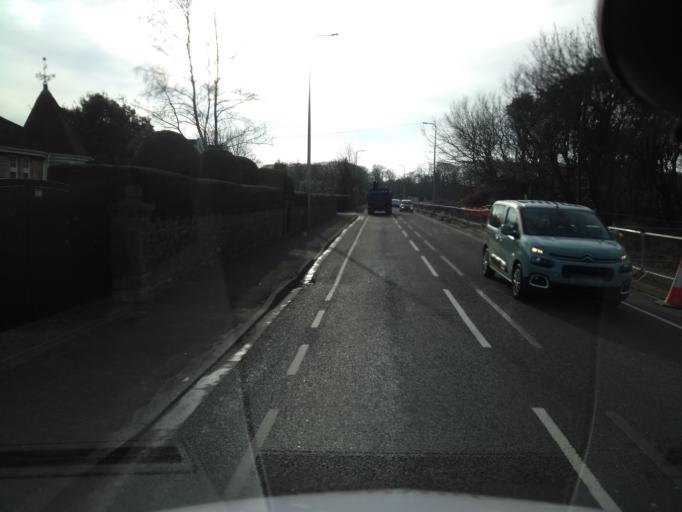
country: GB
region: England
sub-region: North Somerset
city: Weston-super-Mare
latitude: 51.3302
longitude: -2.9806
